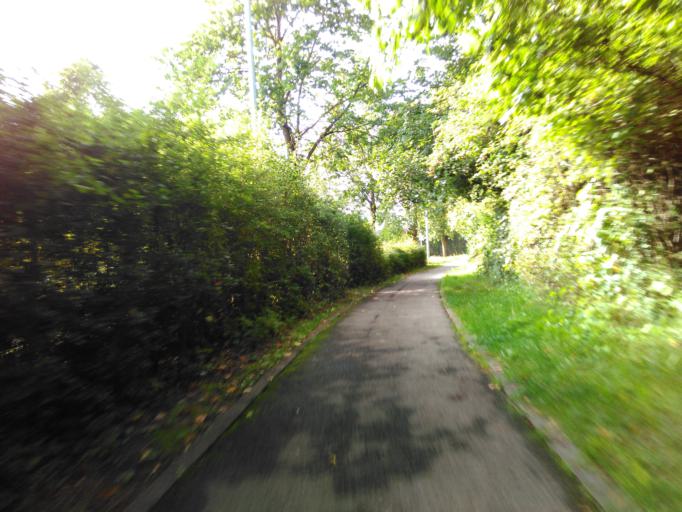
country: LU
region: Luxembourg
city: Belvaux
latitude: 49.5150
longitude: 5.9276
